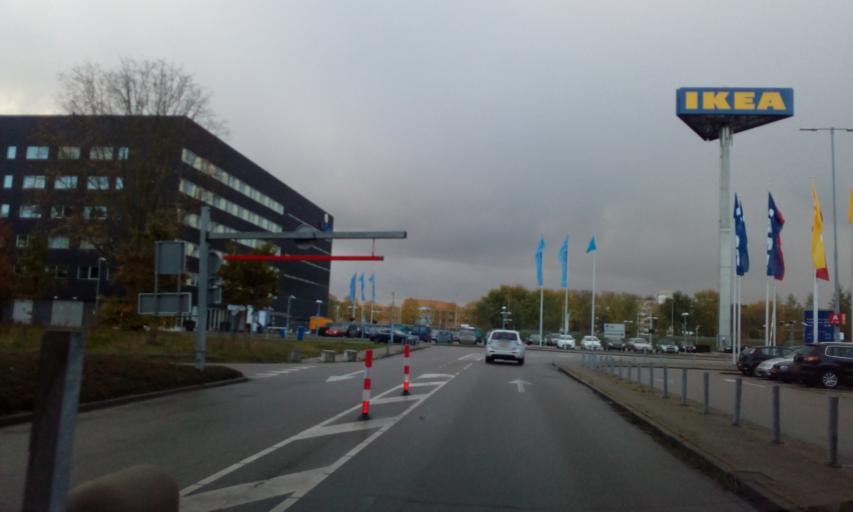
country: NL
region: South Holland
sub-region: Gemeente Delft
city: Delft
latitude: 52.0119
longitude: 4.3819
